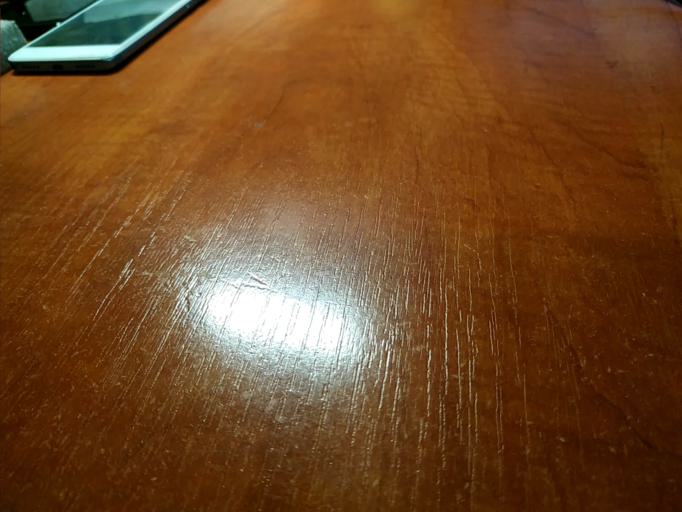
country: RU
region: Kaluga
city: Iznoski
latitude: 54.9628
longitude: 35.4158
